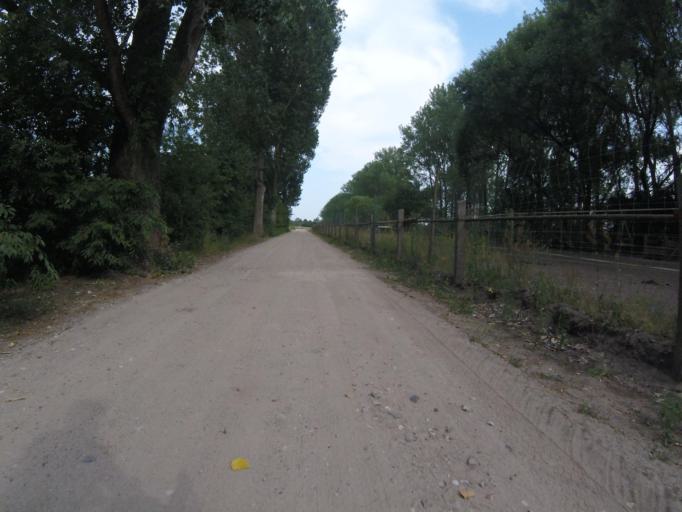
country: DE
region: Brandenburg
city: Erkner
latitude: 52.3055
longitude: 13.7729
